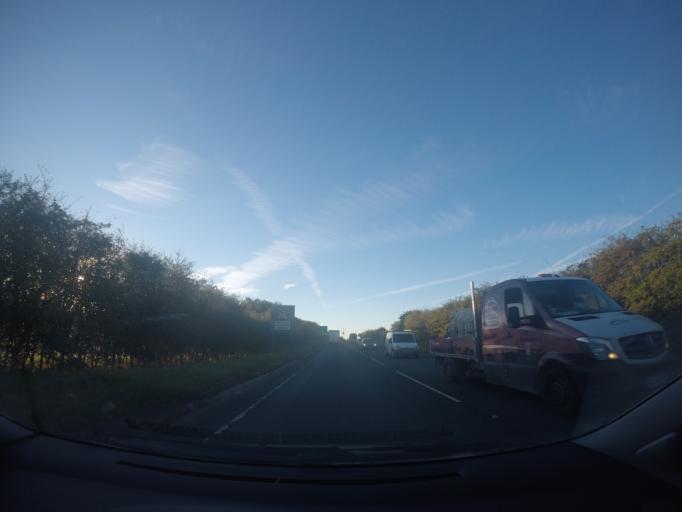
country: GB
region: England
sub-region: City of York
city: Copmanthorpe
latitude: 53.9396
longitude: -1.1452
